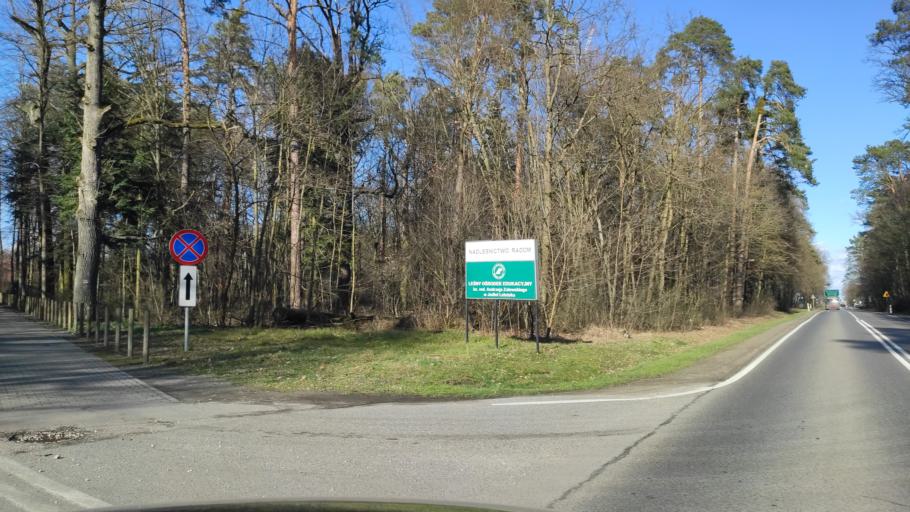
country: PL
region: Masovian Voivodeship
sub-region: Powiat radomski
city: Jedlnia-Letnisko
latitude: 51.4459
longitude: 21.3233
